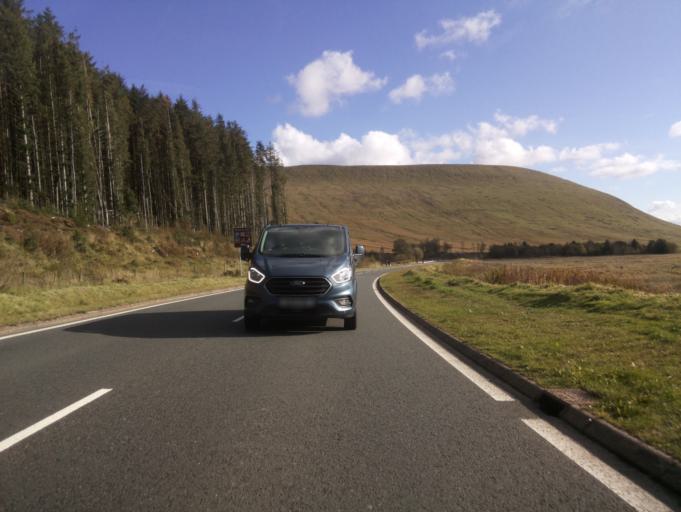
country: GB
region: Wales
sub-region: Sir Powys
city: Brecon
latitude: 51.8713
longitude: -3.4763
